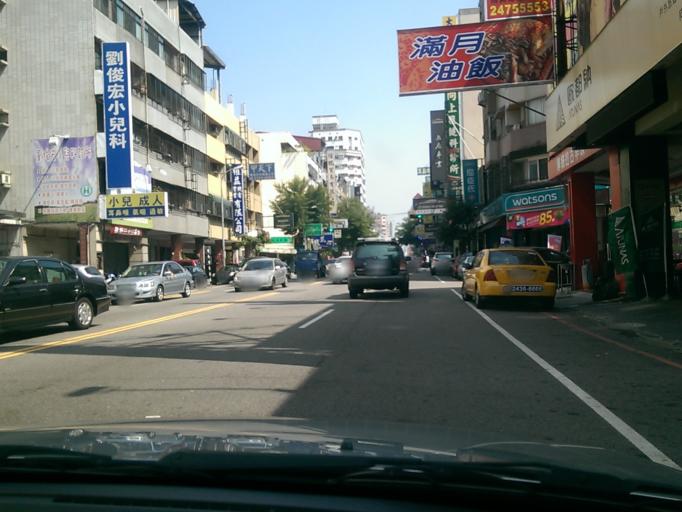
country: TW
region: Taiwan
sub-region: Taichung City
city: Taichung
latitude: 24.1468
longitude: 120.6532
